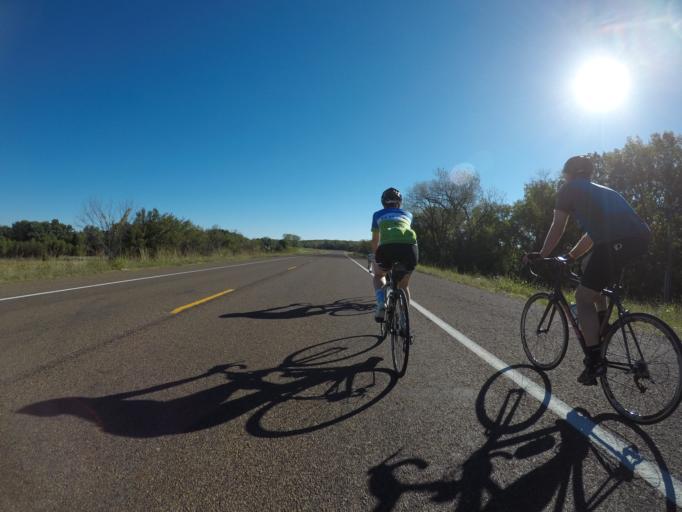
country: US
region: Kansas
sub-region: Johnson County
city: De Soto
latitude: 39.0063
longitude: -95.0262
